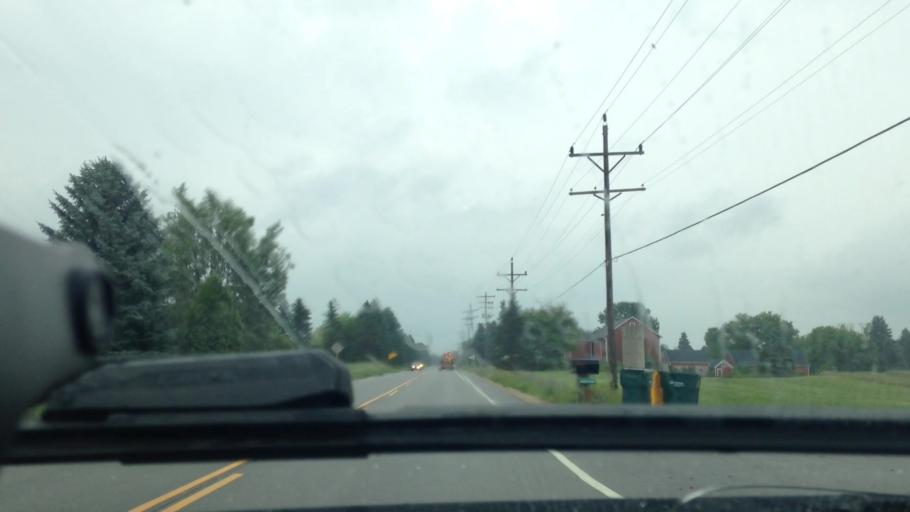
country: US
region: Wisconsin
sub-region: Washington County
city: Slinger
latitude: 43.3209
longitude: -88.2680
